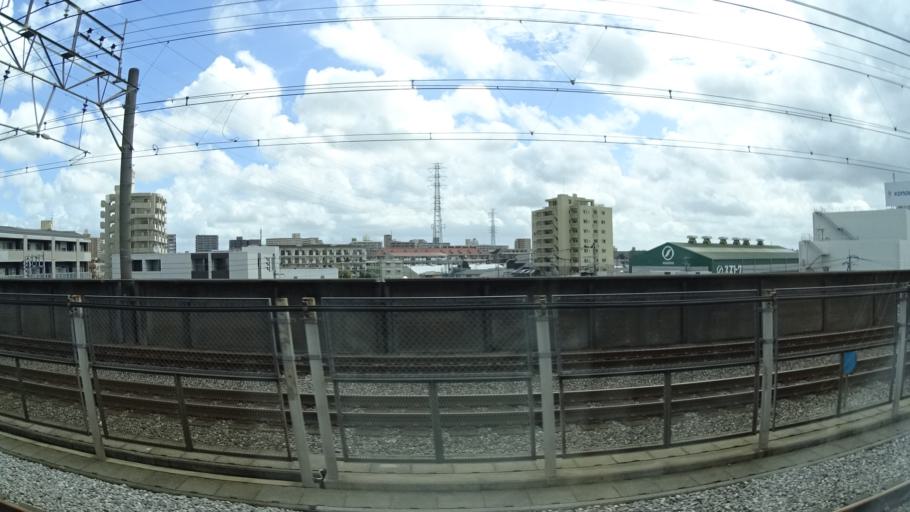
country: JP
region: Saitama
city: Yono
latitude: 35.8420
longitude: 139.6488
